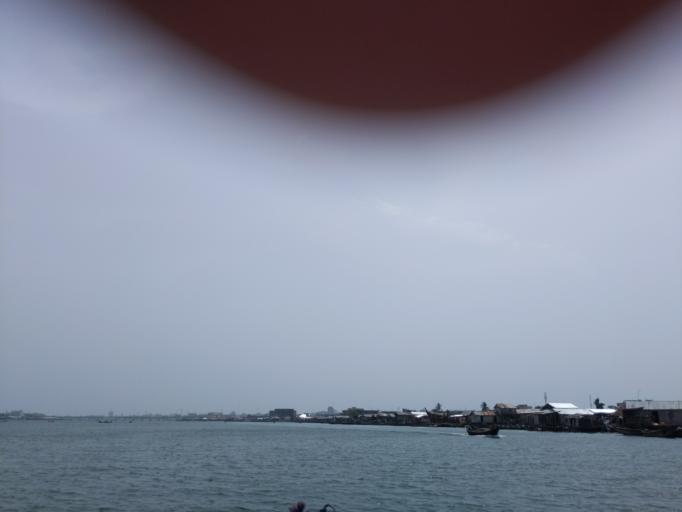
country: BJ
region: Littoral
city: Cotonou
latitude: 6.3865
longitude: 2.4351
